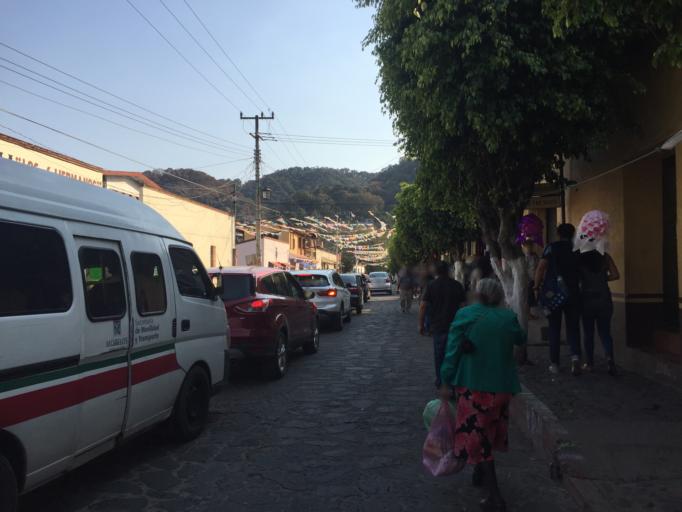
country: MX
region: Morelos
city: Tepoztlan
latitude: 18.9829
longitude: -99.1022
